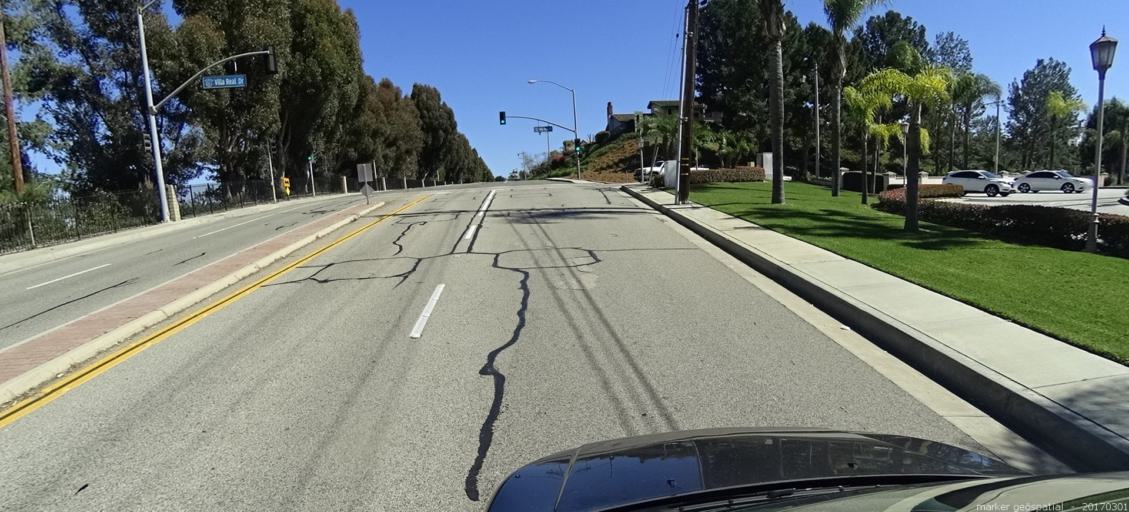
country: US
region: California
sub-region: Orange County
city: Villa Park
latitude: 33.8378
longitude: -117.8226
